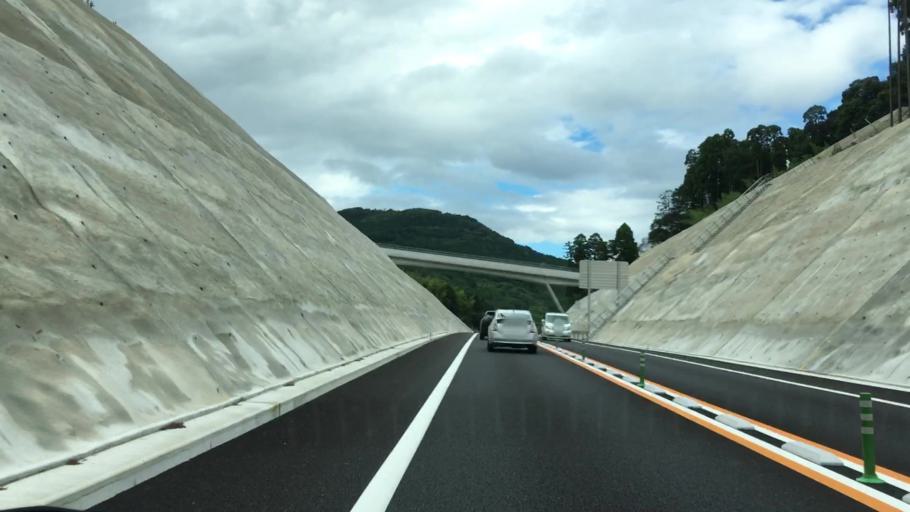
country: JP
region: Saga Prefecture
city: Imaricho-ko
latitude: 33.3056
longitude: 129.9160
